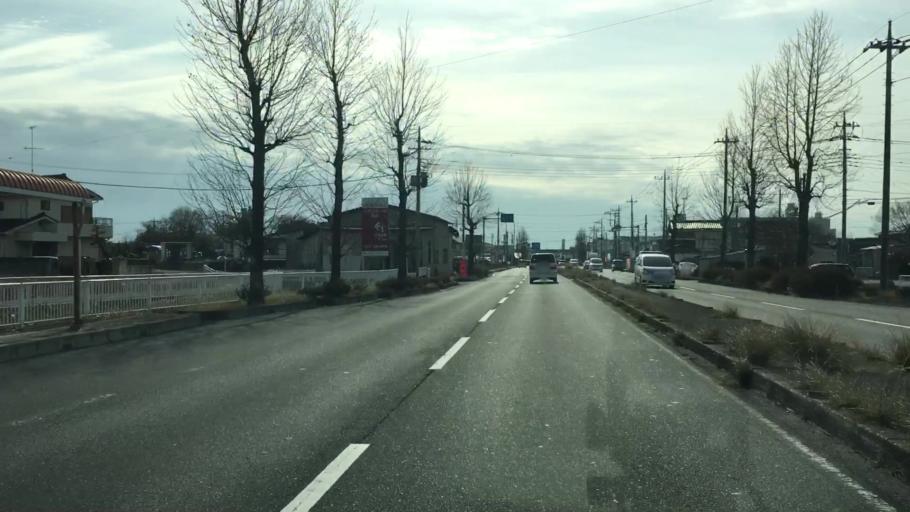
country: JP
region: Saitama
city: Menuma
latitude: 36.1785
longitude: 139.3700
